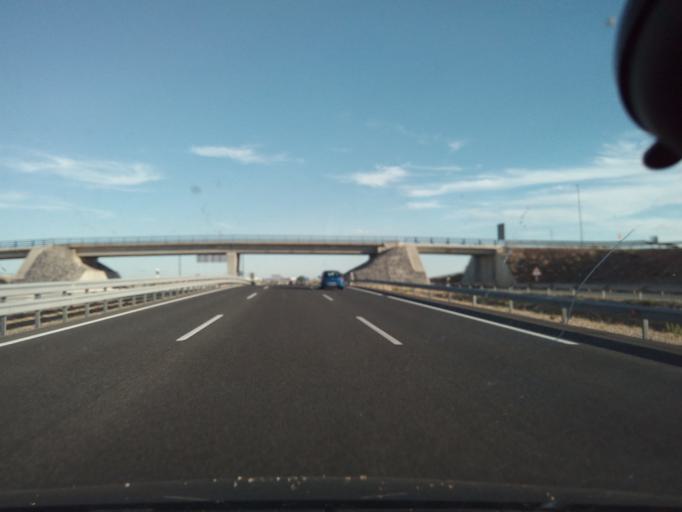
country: ES
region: Castille-La Mancha
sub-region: Province of Toledo
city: Dosbarrios
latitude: 39.9113
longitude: -3.4759
